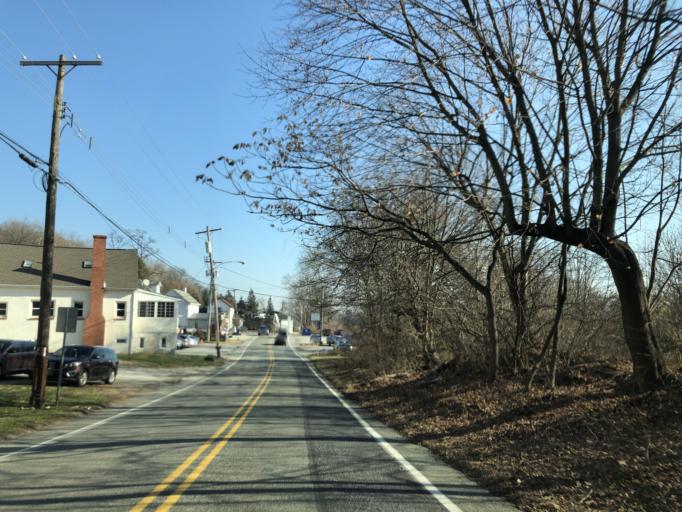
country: US
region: Pennsylvania
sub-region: Chester County
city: Malvern
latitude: 40.0728
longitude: -75.5250
